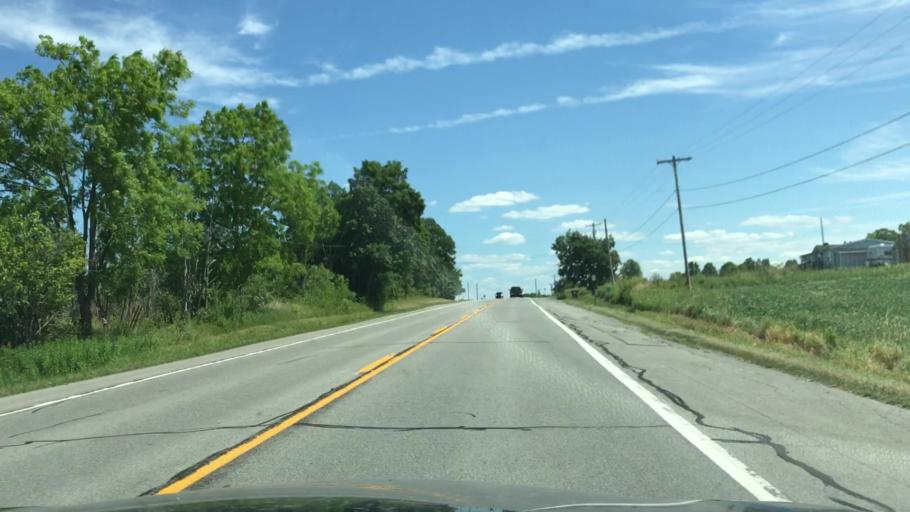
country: US
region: New York
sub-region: Livingston County
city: Mount Morris
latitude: 42.6750
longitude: -77.8157
